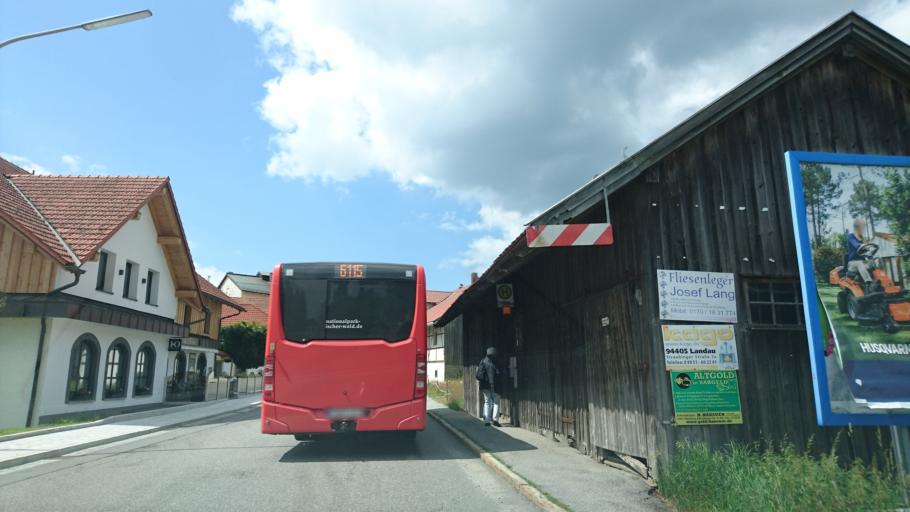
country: DE
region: Bavaria
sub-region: Lower Bavaria
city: Mauth
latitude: 48.8900
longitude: 13.5851
